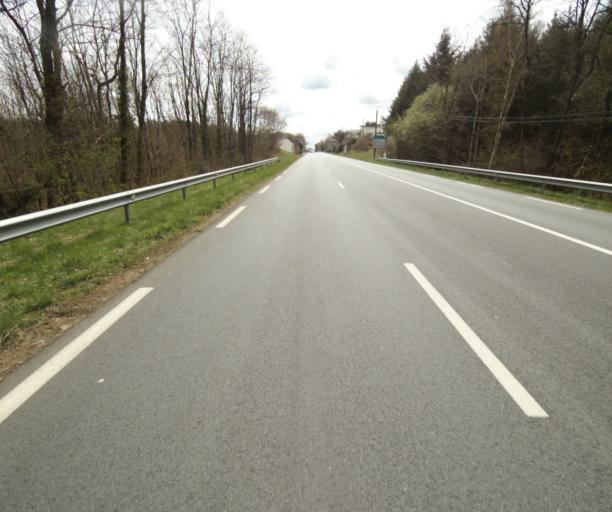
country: FR
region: Limousin
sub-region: Departement de la Correze
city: Sainte-Fortunade
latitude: 45.2037
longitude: 1.8290
